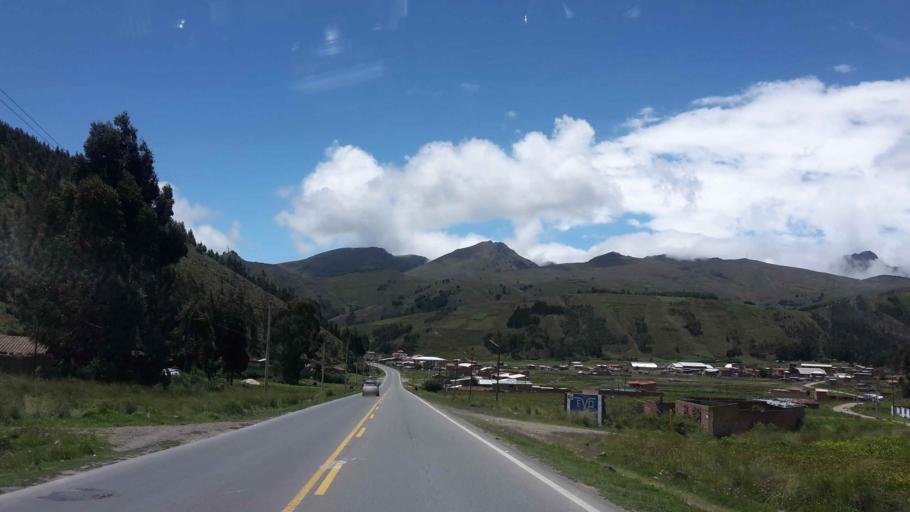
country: BO
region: Cochabamba
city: Colomi
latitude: -17.3804
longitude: -65.8345
